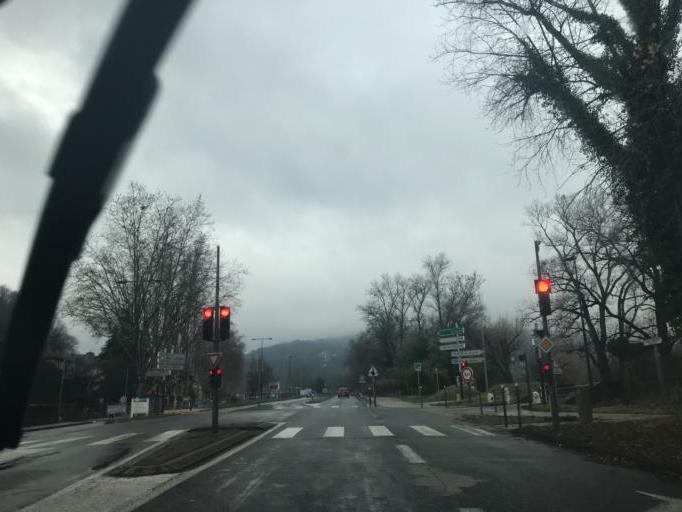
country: FR
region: Rhone-Alpes
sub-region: Departement du Rhone
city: Rochetaillee-sur-Saone
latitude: 45.8452
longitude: 4.8352
